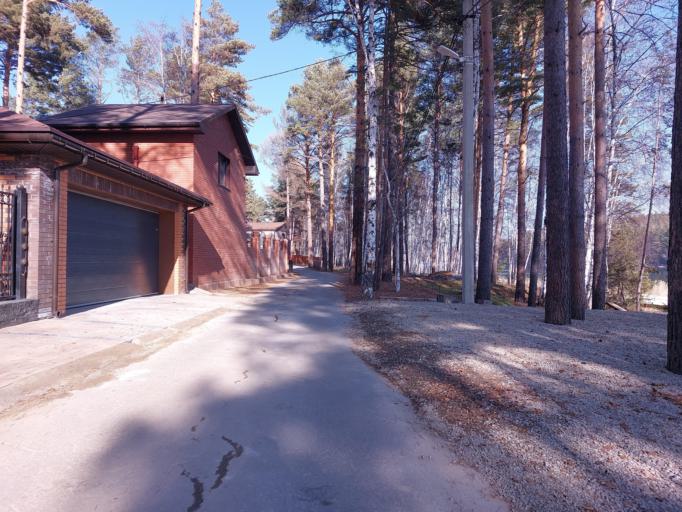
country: RU
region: Irkutsk
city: Pivovarikha
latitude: 52.1885
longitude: 104.4669
